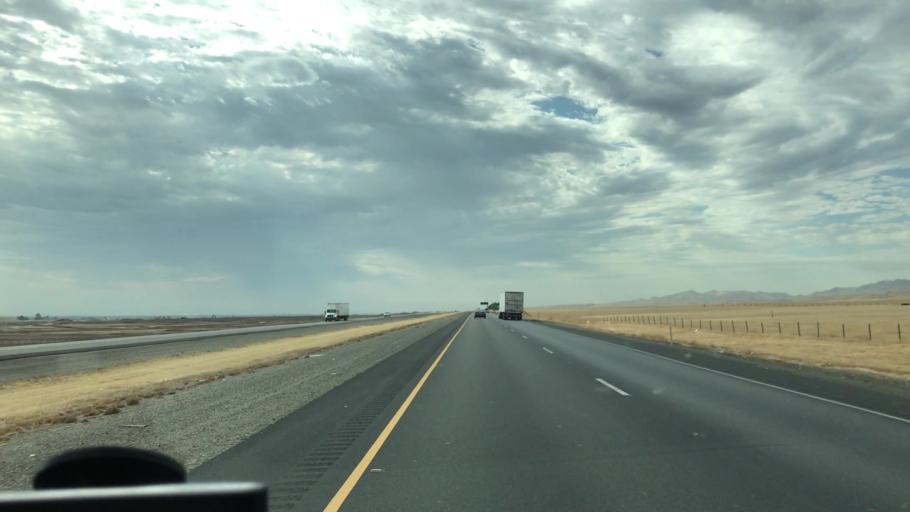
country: US
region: California
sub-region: San Joaquin County
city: Tracy
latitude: 37.6848
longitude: -121.4784
